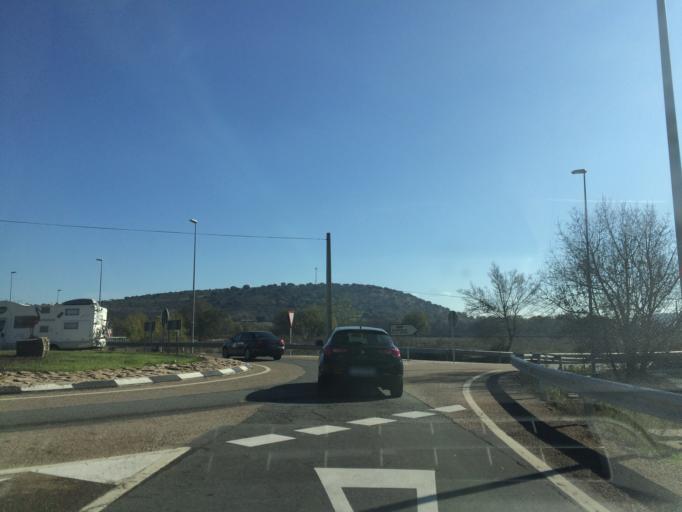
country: ES
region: Madrid
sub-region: Provincia de Madrid
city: Guadalix de la Sierra
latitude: 40.7932
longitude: -3.6924
